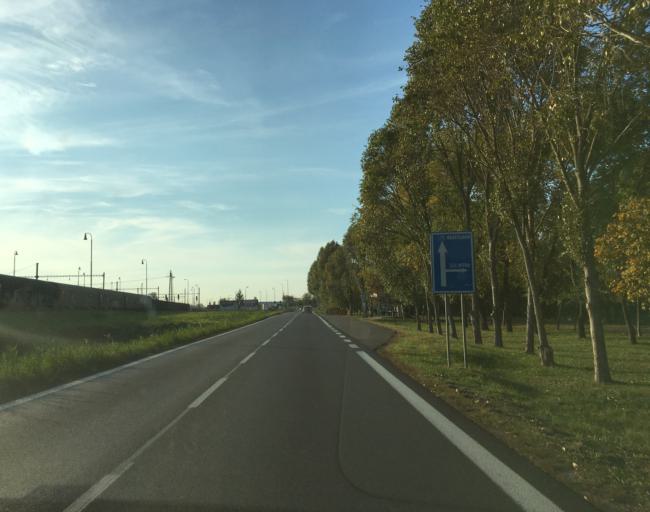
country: SK
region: Nitriansky
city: Sellye
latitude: 48.1527
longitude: 17.9317
